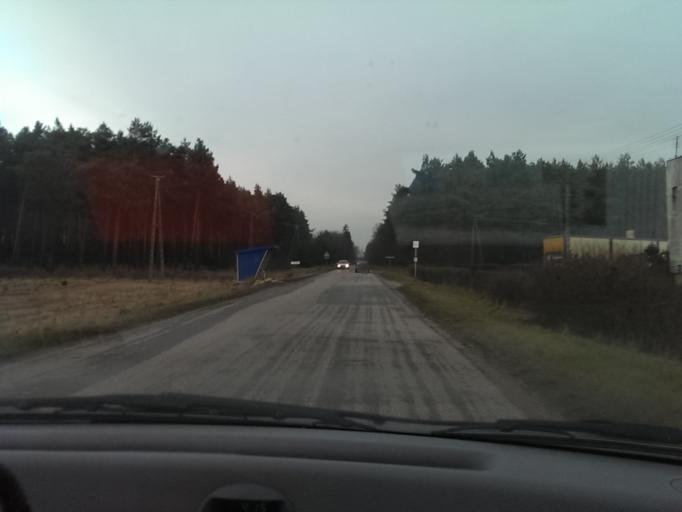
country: PL
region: Kujawsko-Pomorskie
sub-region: Powiat nakielski
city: Szubin
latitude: 53.0759
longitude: 17.7259
